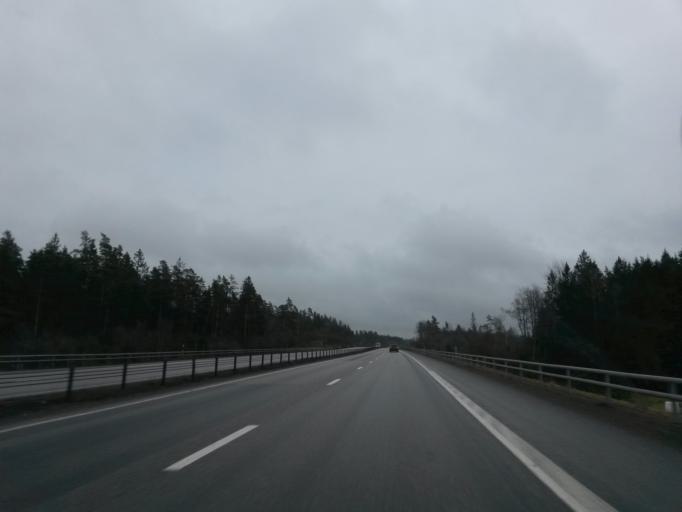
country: SE
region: Vaestra Goetaland
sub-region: Uddevalla Kommun
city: Uddevalla
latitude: 58.3336
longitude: 12.0058
